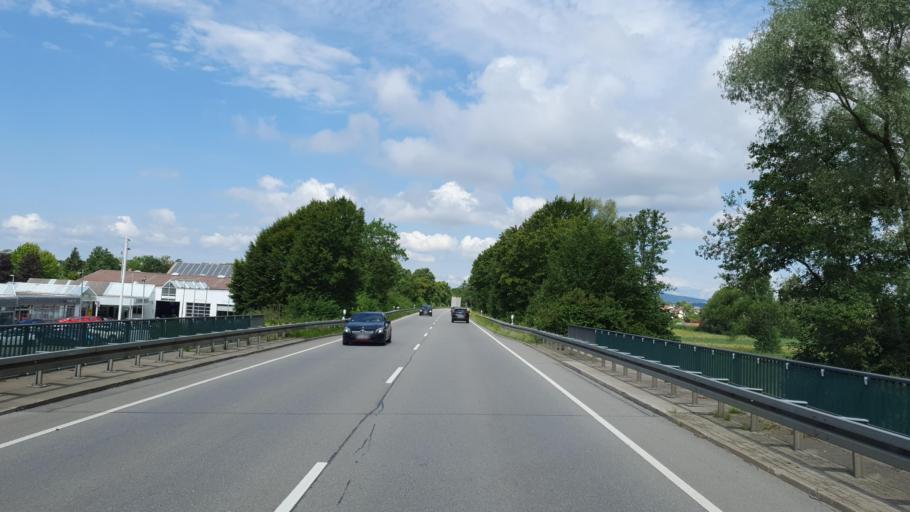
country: DE
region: Baden-Wuerttemberg
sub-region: Tuebingen Region
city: Friedrichshafen
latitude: 47.6513
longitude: 9.5058
